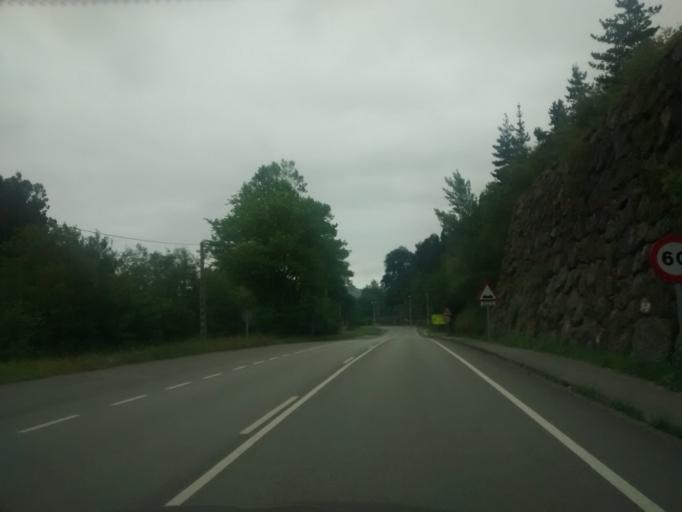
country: ES
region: Cantabria
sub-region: Provincia de Cantabria
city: Cabezon de la Sal
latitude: 43.2816
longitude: -4.2364
